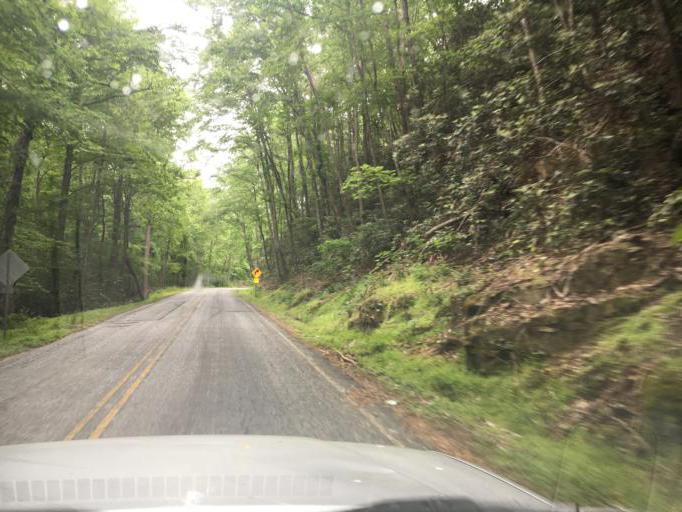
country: US
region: South Carolina
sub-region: Greenville County
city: Tigerville
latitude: 35.1291
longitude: -82.3833
